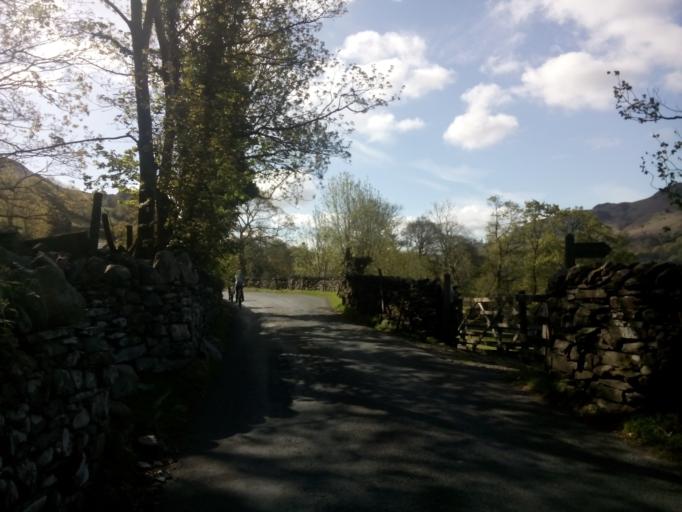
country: GB
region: England
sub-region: Cumbria
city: Ambleside
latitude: 54.4466
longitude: -3.0628
